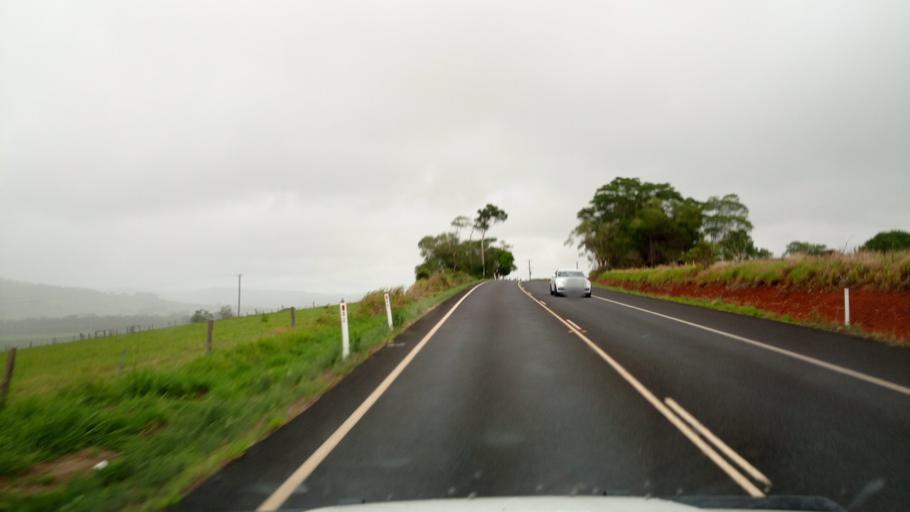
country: AU
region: Queensland
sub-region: Tablelands
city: Atherton
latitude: -17.2810
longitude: 145.5970
